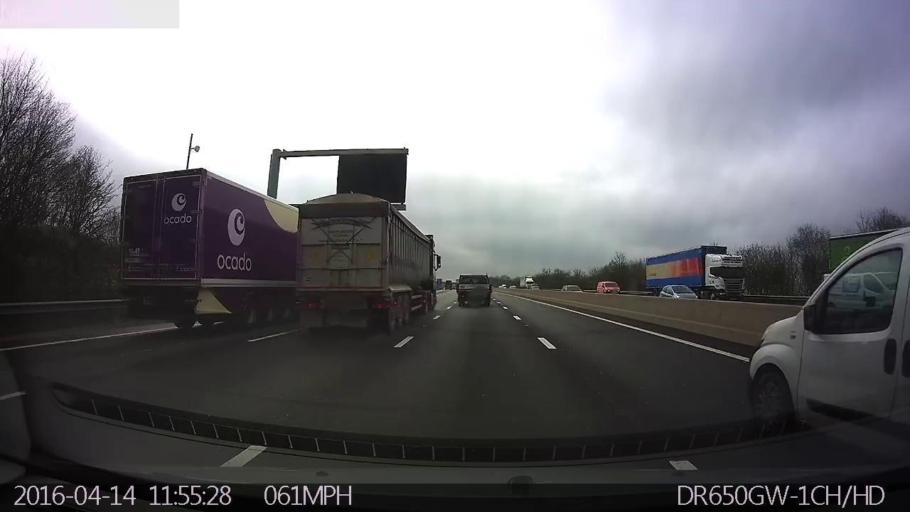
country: GB
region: England
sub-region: Derbyshire
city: Tibshelf
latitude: 53.1444
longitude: -1.3307
